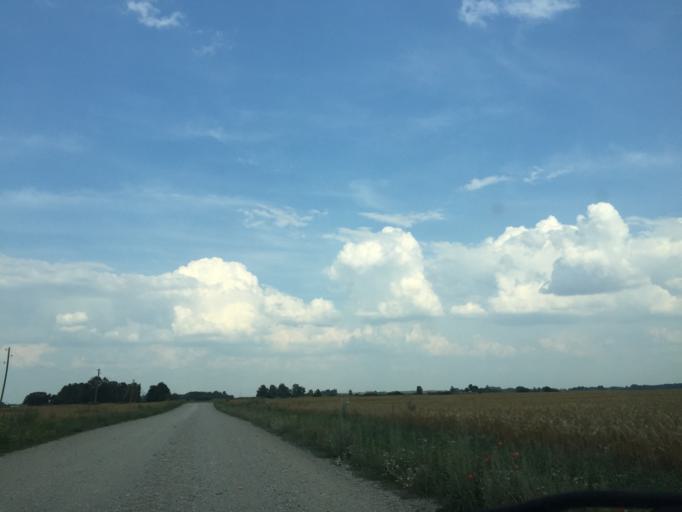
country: LT
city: Zagare
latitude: 56.4152
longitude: 23.1741
